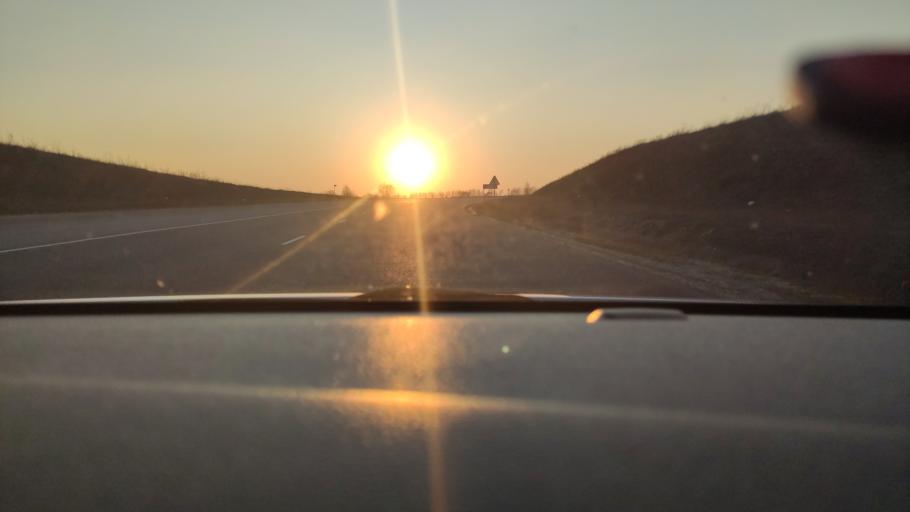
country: RU
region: Voronezj
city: Kolodeznyy
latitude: 51.3279
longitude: 39.1494
